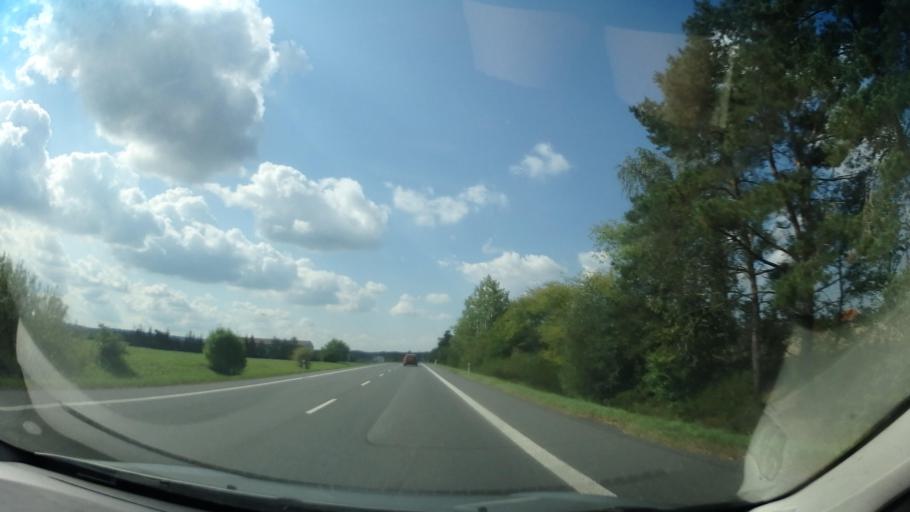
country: CZ
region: Central Bohemia
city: Kostelec nad Cernymi Lesy
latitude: 49.9853
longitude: 14.8552
